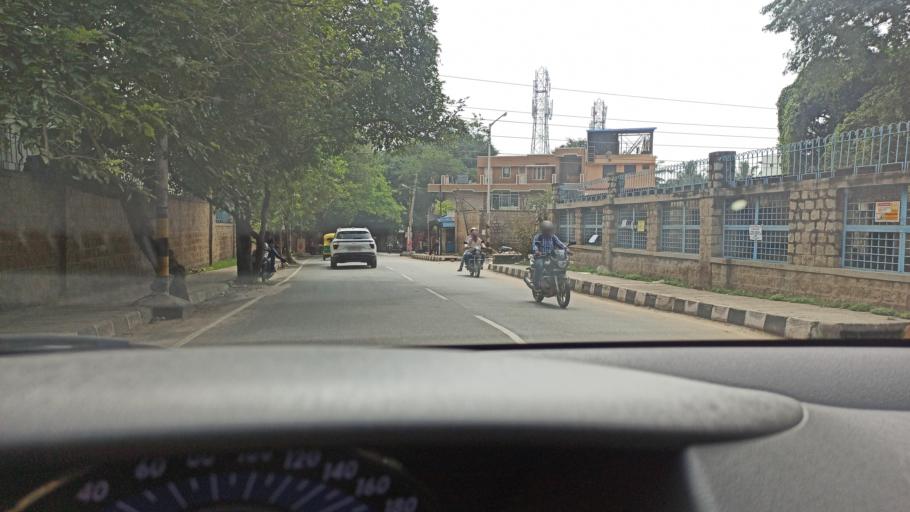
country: IN
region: Karnataka
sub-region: Bangalore Urban
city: Bangalore
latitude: 12.9861
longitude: 77.6791
